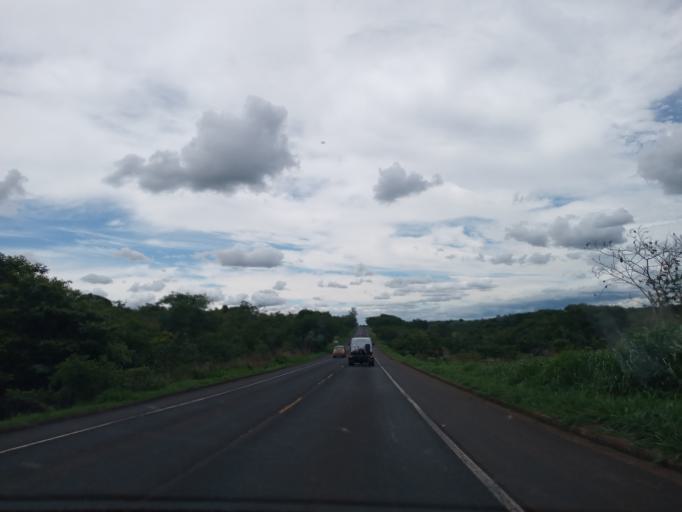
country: BR
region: Minas Gerais
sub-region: Uberlandia
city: Uberlandia
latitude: -19.1849
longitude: -47.8759
